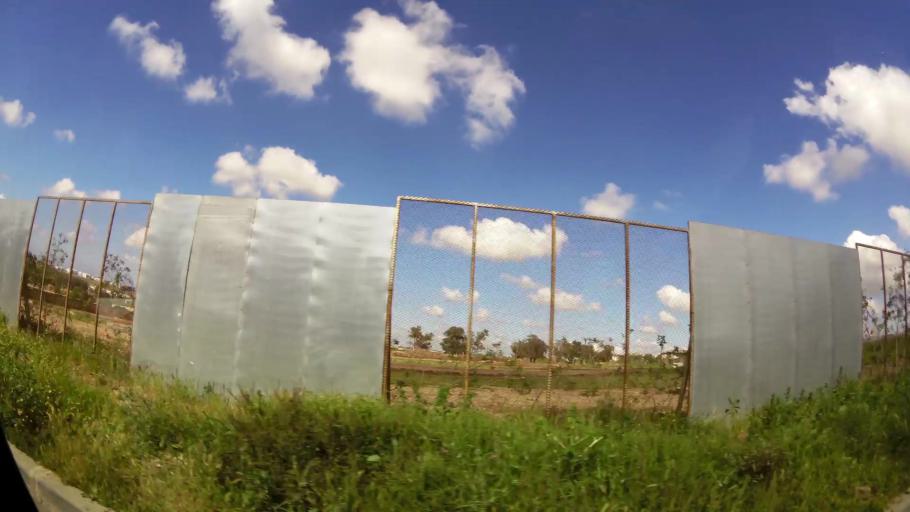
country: MA
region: Grand Casablanca
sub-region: Nouaceur
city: Bouskoura
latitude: 33.4721
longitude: -7.6149
